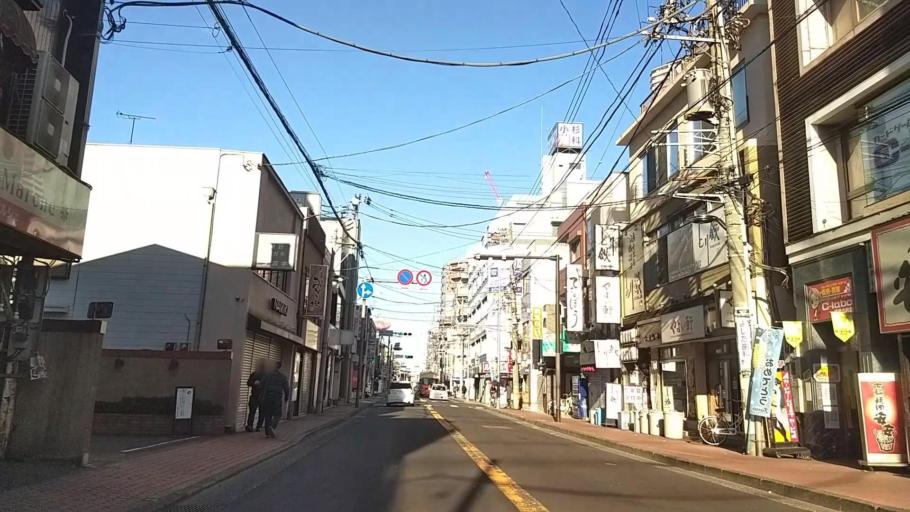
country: JP
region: Kanagawa
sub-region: Kawasaki-shi
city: Kawasaki
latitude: 35.5735
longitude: 139.6584
